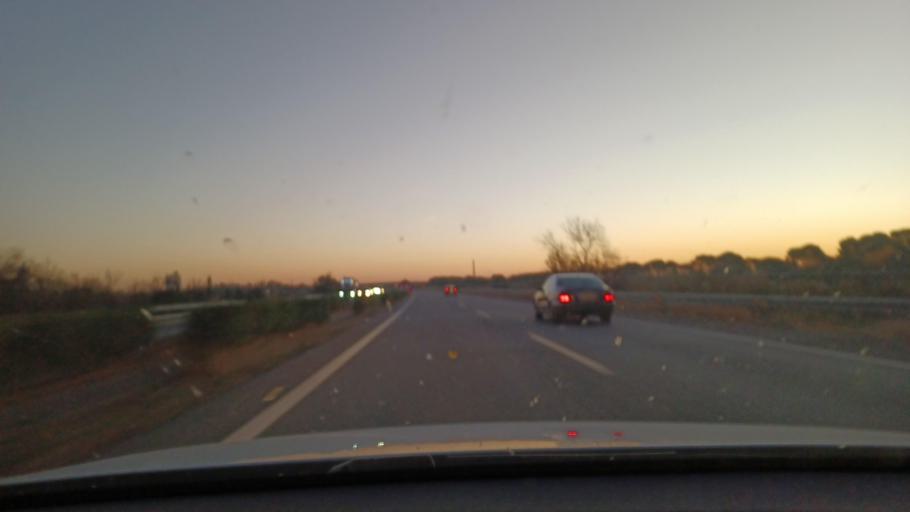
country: ES
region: Catalonia
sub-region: Provincia de Tarragona
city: Cambrils
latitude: 41.0859
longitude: 1.0734
